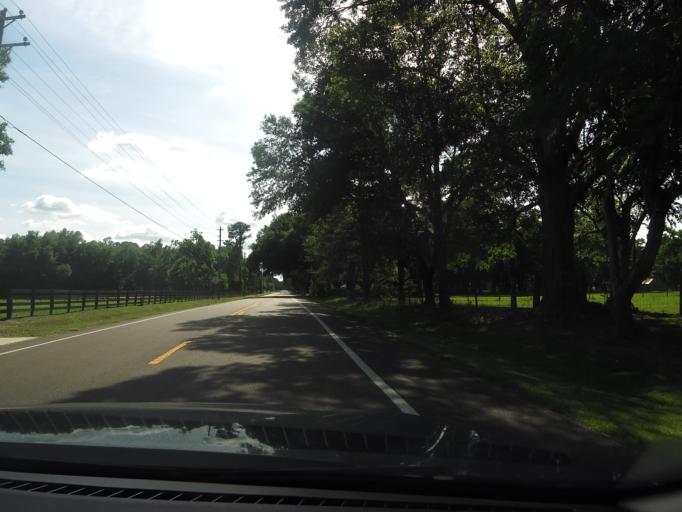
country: US
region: Florida
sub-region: Nassau County
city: Callahan
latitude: 30.5599
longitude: -81.8572
